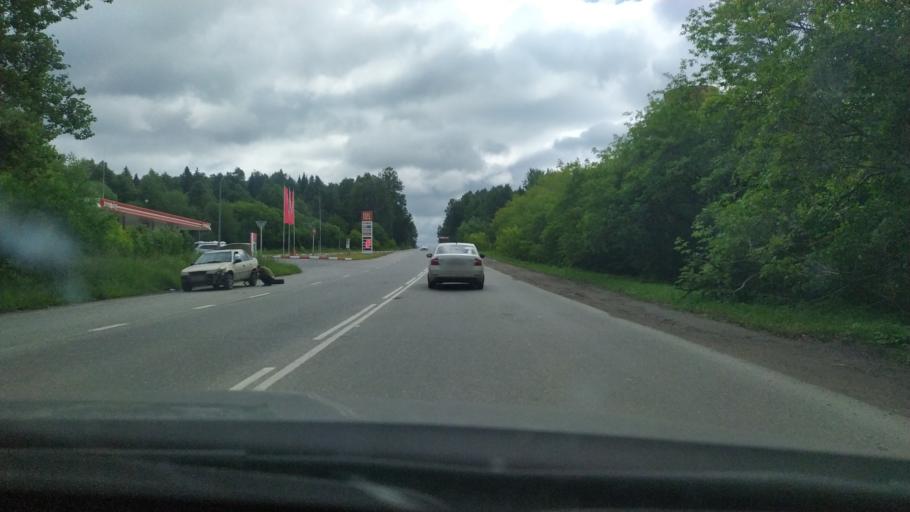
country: RU
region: Perm
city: Ferma
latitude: 57.9750
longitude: 56.3277
